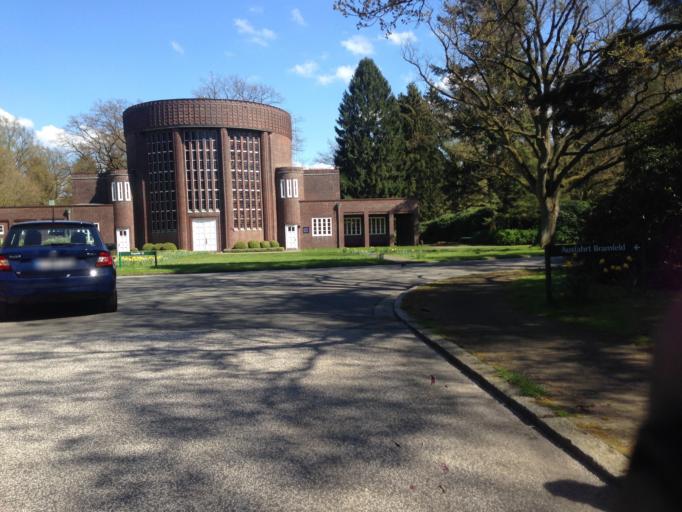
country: DE
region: Hamburg
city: Wellingsbuettel
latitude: 53.6244
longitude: 10.0762
